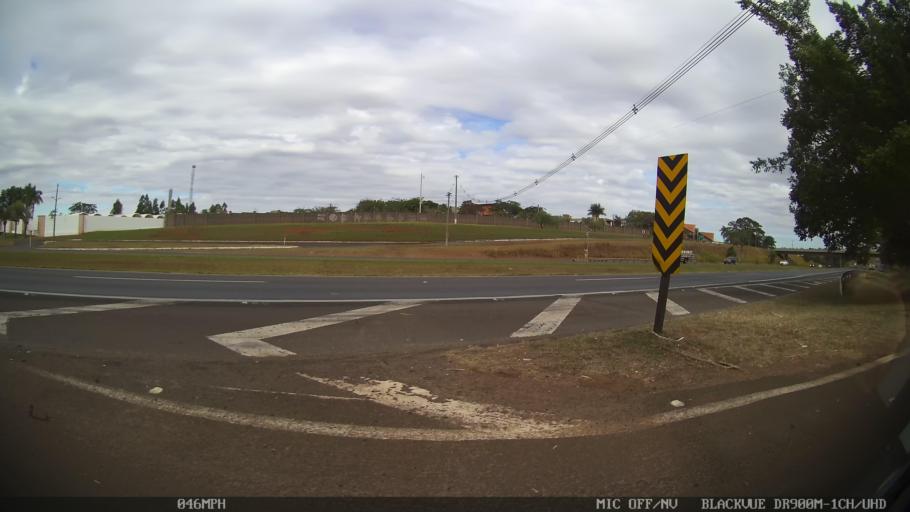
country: BR
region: Sao Paulo
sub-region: Sao Jose Do Rio Preto
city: Sao Jose do Rio Preto
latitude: -20.8158
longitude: -49.4478
